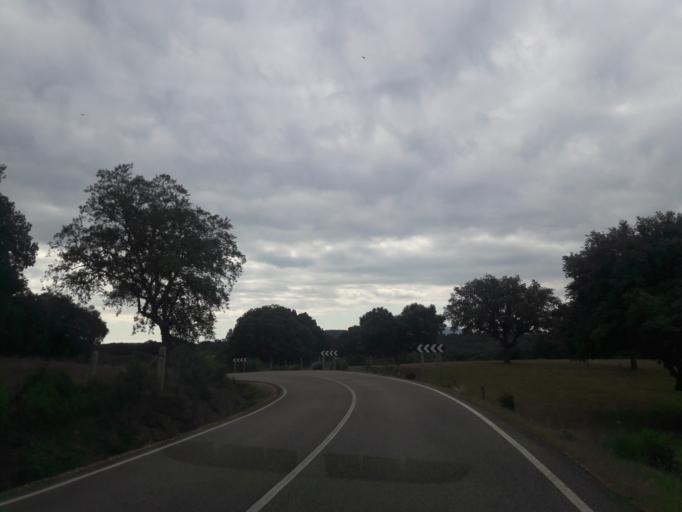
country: ES
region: Castille and Leon
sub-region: Provincia de Salamanca
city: Zamarra
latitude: 40.5364
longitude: -6.4142
